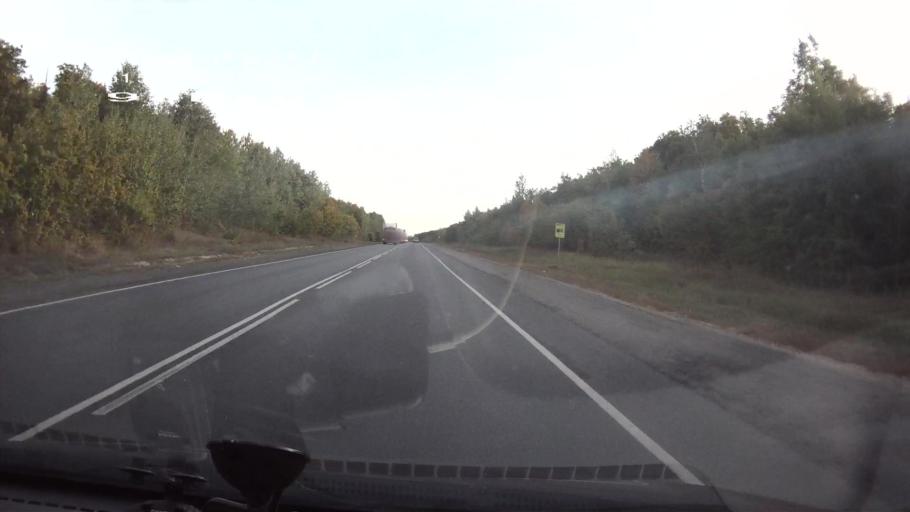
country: RU
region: Saratov
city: Sokolovyy
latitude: 51.5748
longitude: 45.7643
